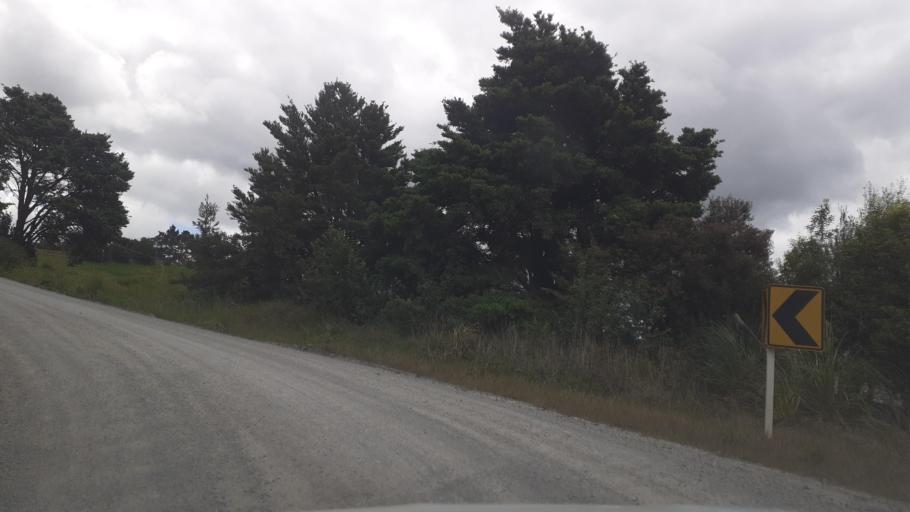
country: NZ
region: Northland
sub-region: Far North District
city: Moerewa
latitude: -35.3891
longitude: 173.9974
